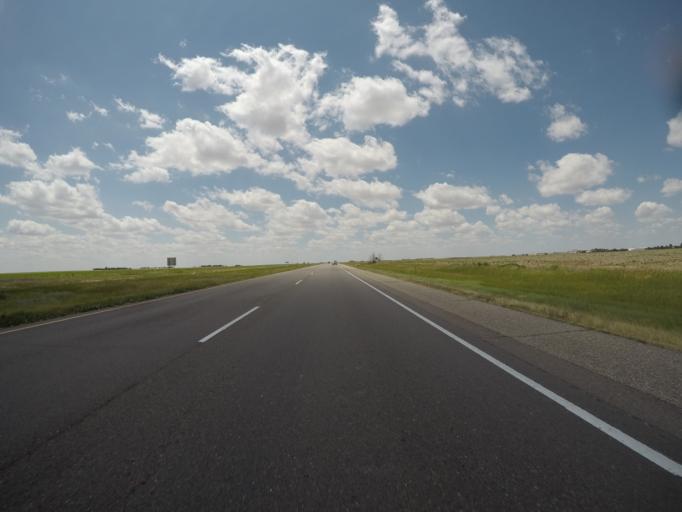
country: US
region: Colorado
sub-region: Kit Carson County
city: Burlington
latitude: 39.2943
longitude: -102.3012
